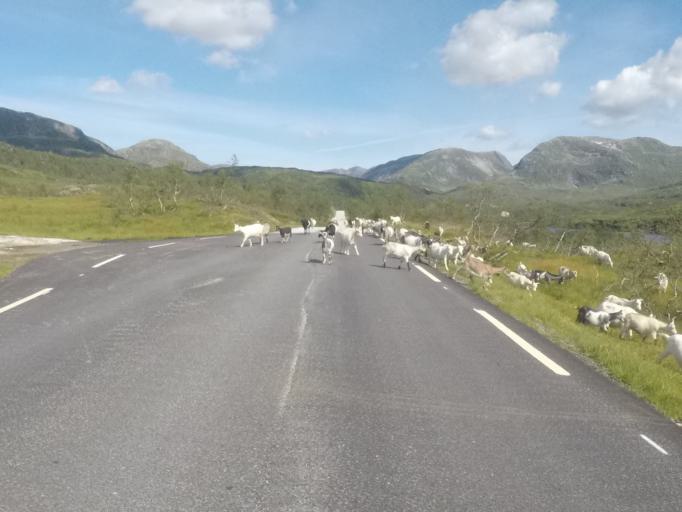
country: NO
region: Sogn og Fjordane
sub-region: Balestrand
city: Balestrand
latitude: 61.3343
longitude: 6.3829
